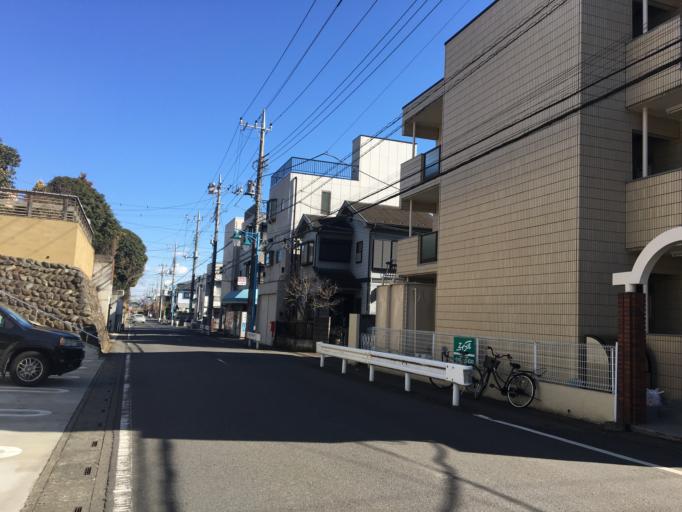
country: JP
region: Saitama
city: Kamifukuoka
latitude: 35.8813
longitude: 139.5006
